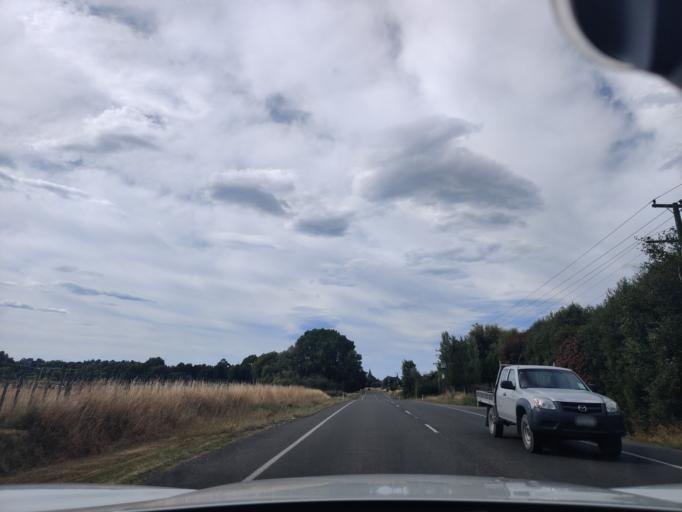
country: NZ
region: Wellington
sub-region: Masterton District
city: Masterton
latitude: -40.9236
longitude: 175.6706
